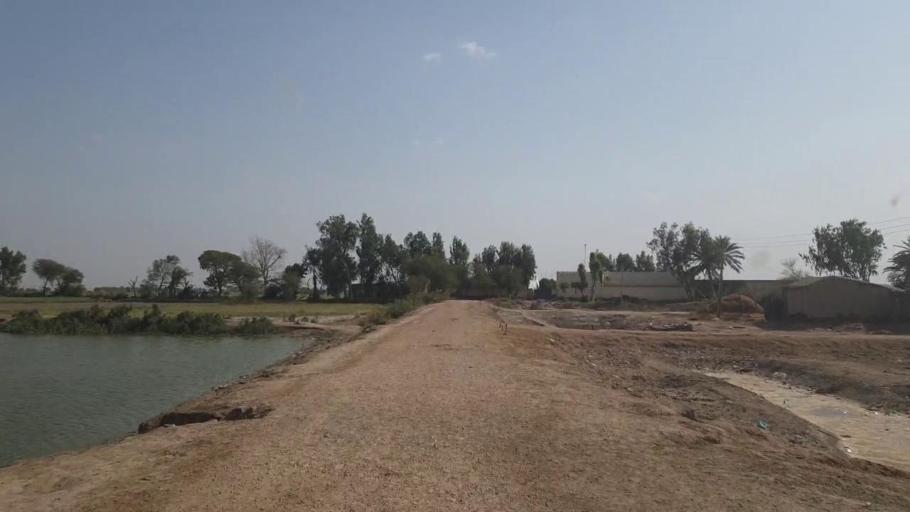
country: PK
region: Sindh
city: Jati
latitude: 24.5133
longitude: 68.5256
